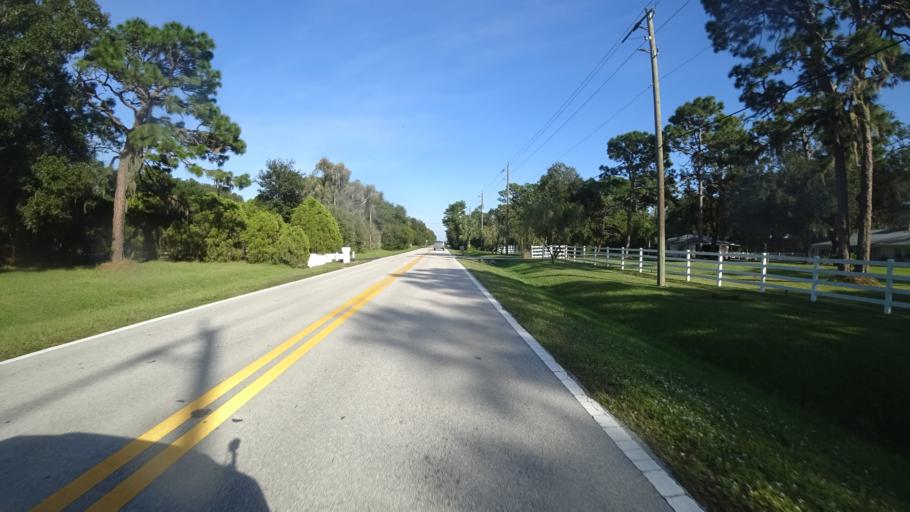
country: US
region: Florida
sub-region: Sarasota County
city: North Sarasota
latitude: 27.3817
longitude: -82.5211
